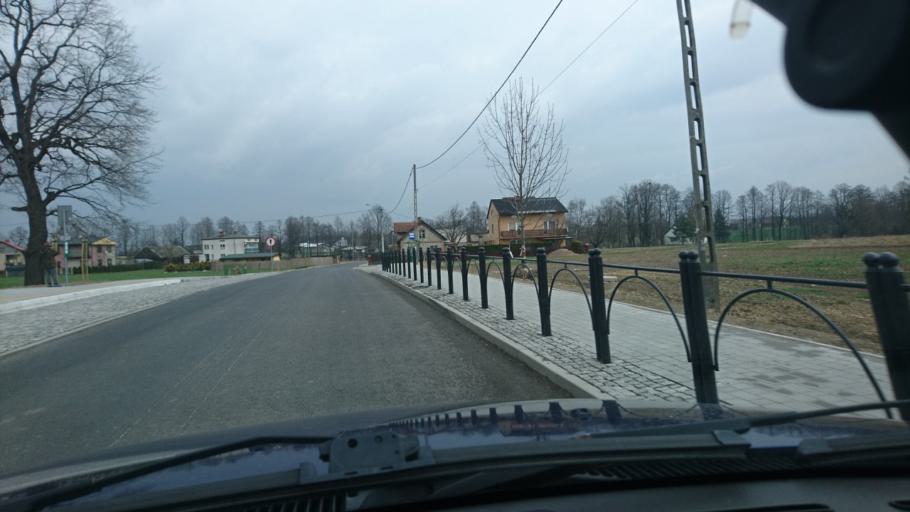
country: PL
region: Silesian Voivodeship
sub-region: Powiat bielski
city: Bronow
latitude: 49.8777
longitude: 18.9218
